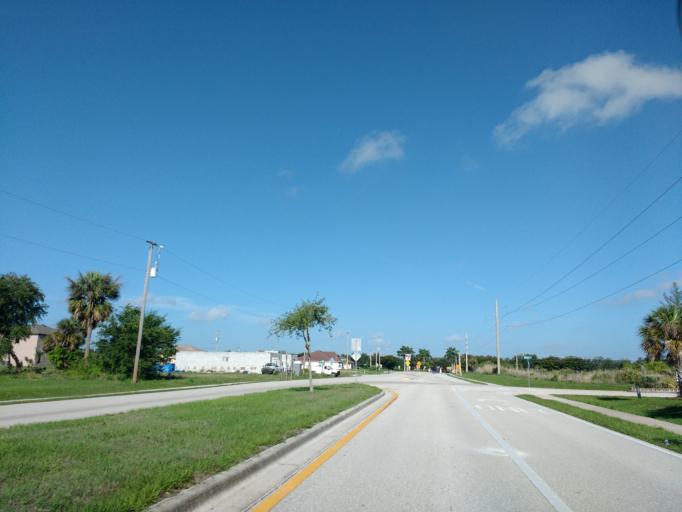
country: US
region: Florida
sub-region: Lee County
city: Cape Coral
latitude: 26.6228
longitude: -82.0209
